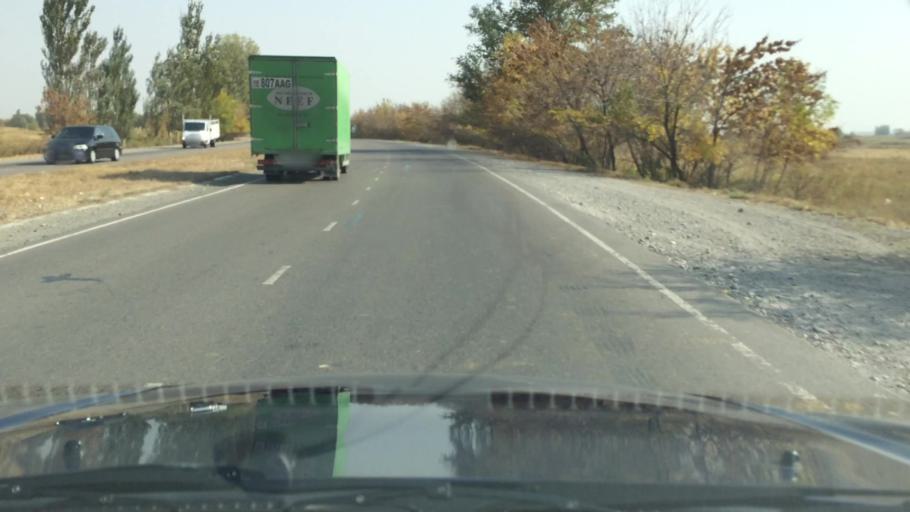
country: KG
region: Chuy
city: Lebedinovka
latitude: 42.9231
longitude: 74.7574
